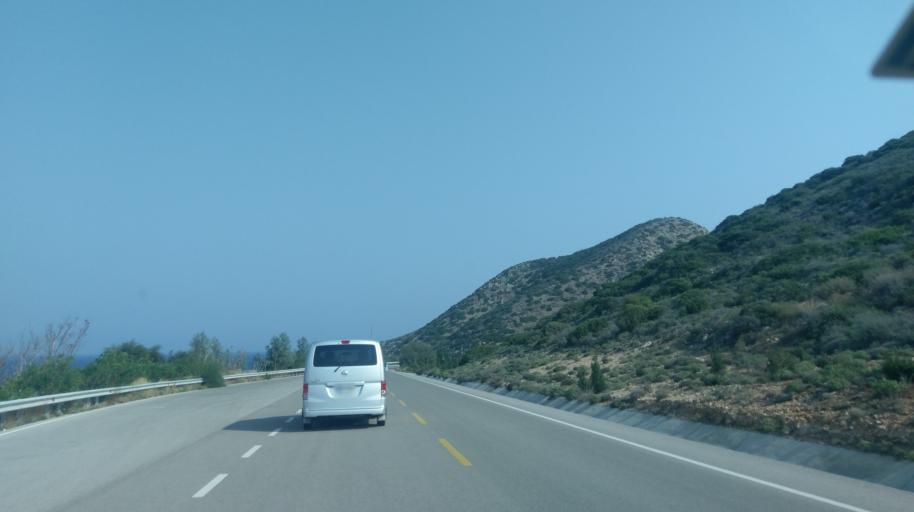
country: CY
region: Ammochostos
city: Leonarisso
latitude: 35.4595
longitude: 34.0116
